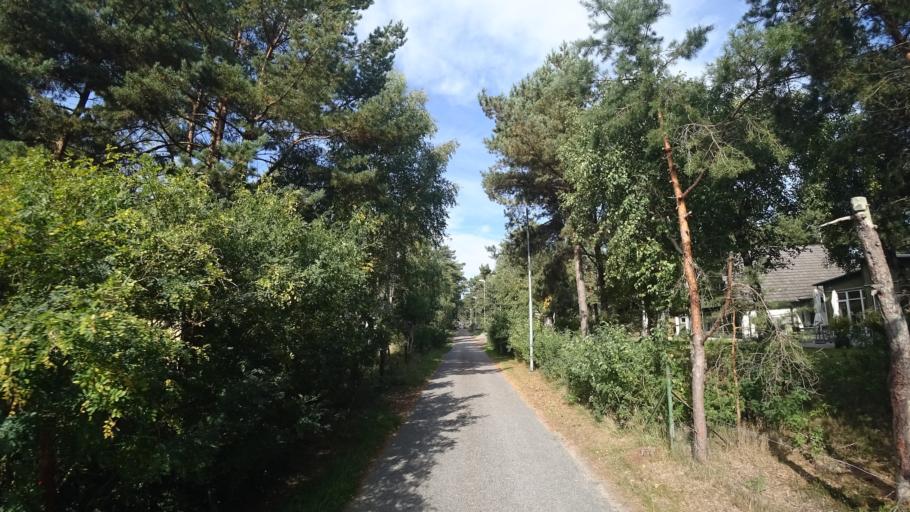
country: SE
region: Skane
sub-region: Kristianstads Kommun
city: Ahus
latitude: 55.9160
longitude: 14.3019
